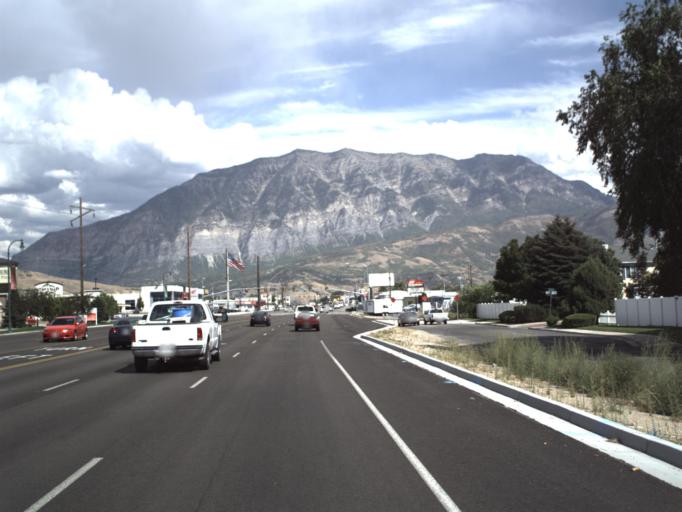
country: US
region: Utah
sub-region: Utah County
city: Orem
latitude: 40.3120
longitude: -111.7136
